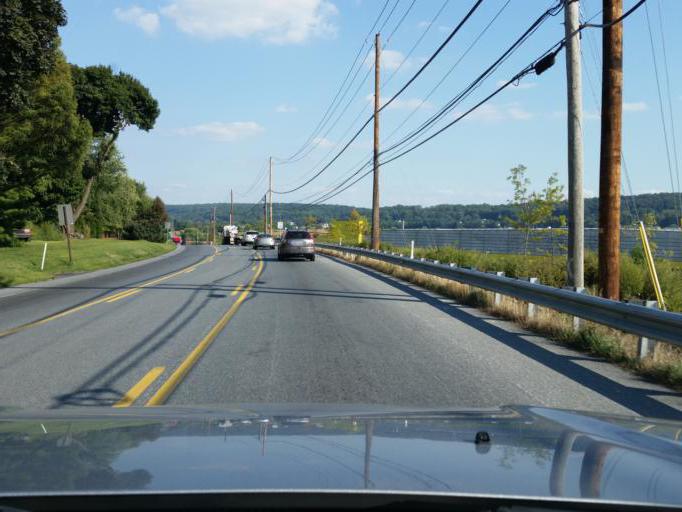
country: US
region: Pennsylvania
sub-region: Lancaster County
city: Gap
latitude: 39.9964
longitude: -76.0483
